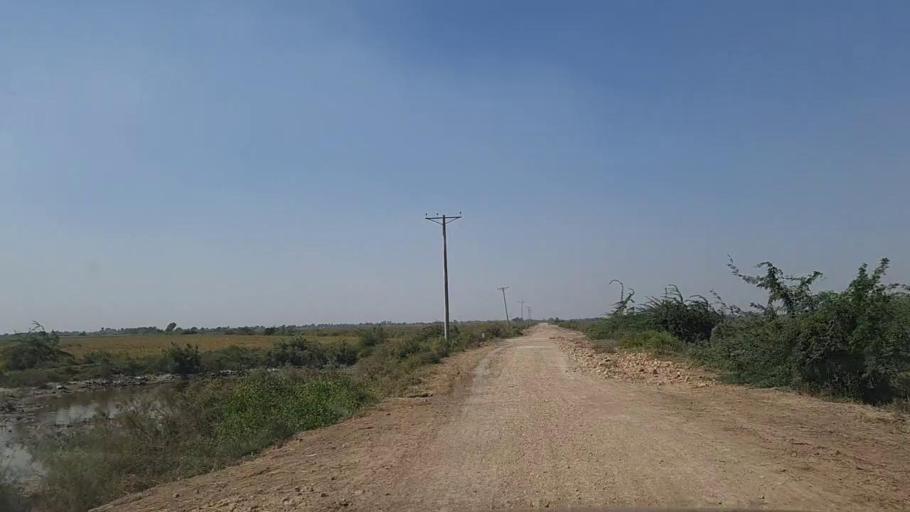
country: PK
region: Sindh
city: Daro Mehar
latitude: 24.8337
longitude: 68.1707
